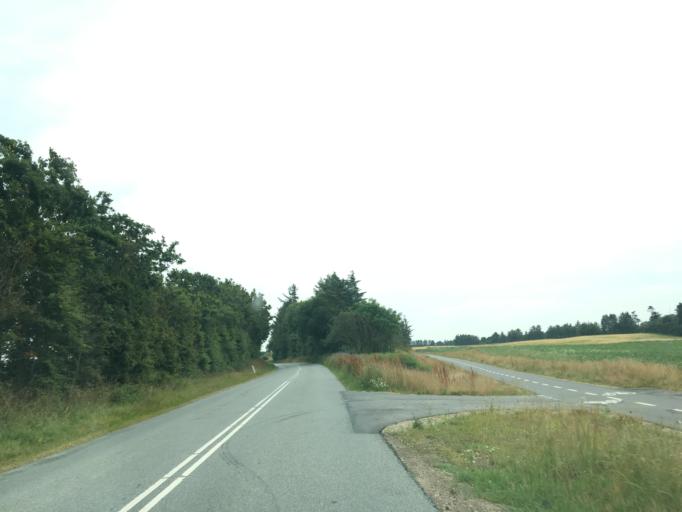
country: DK
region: North Denmark
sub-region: Thisted Kommune
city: Hurup
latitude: 56.8000
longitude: 8.4108
